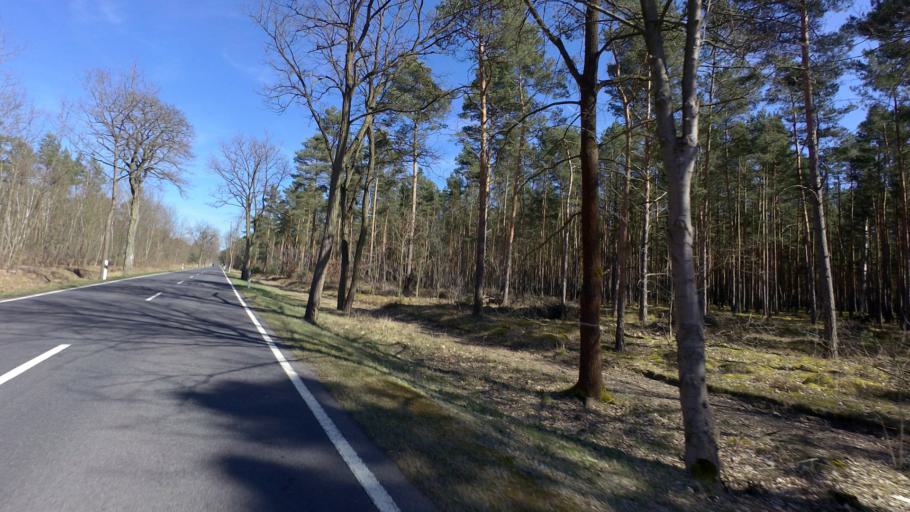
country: DE
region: Brandenburg
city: Storkow
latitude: 52.2061
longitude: 13.9283
